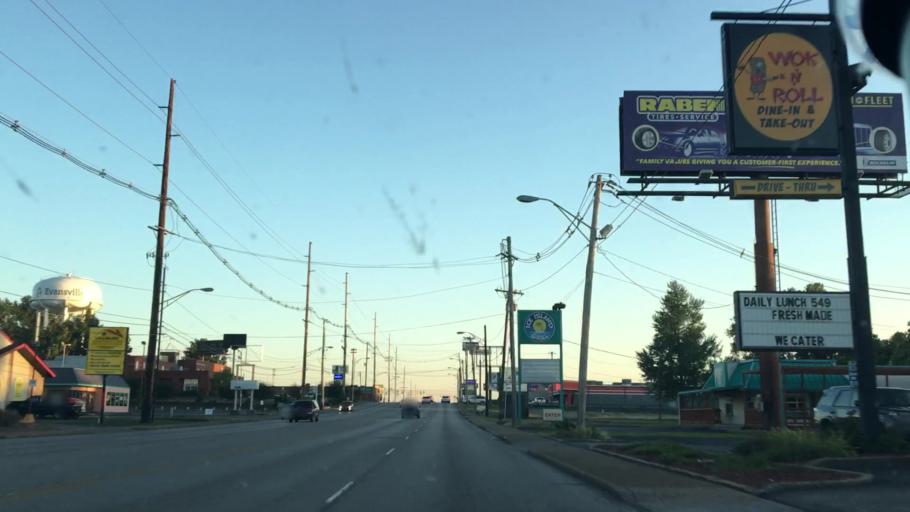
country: US
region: Indiana
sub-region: Vanderburgh County
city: Melody Hill
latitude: 37.9728
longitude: -87.4927
